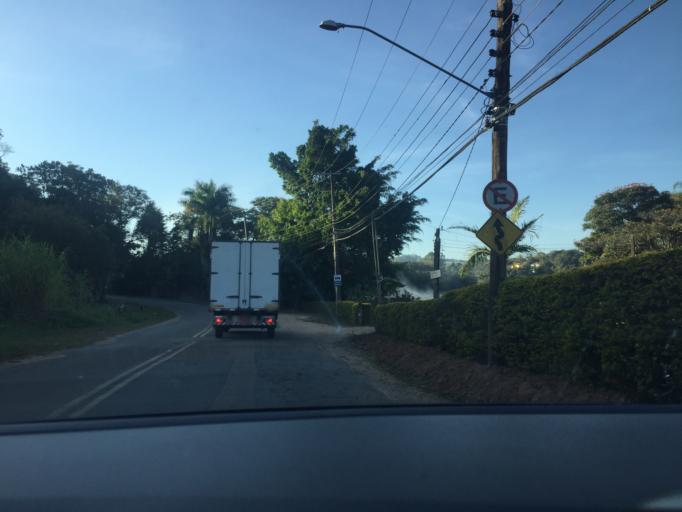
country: BR
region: Sao Paulo
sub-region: Louveira
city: Louveira
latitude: -23.1144
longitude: -46.9166
